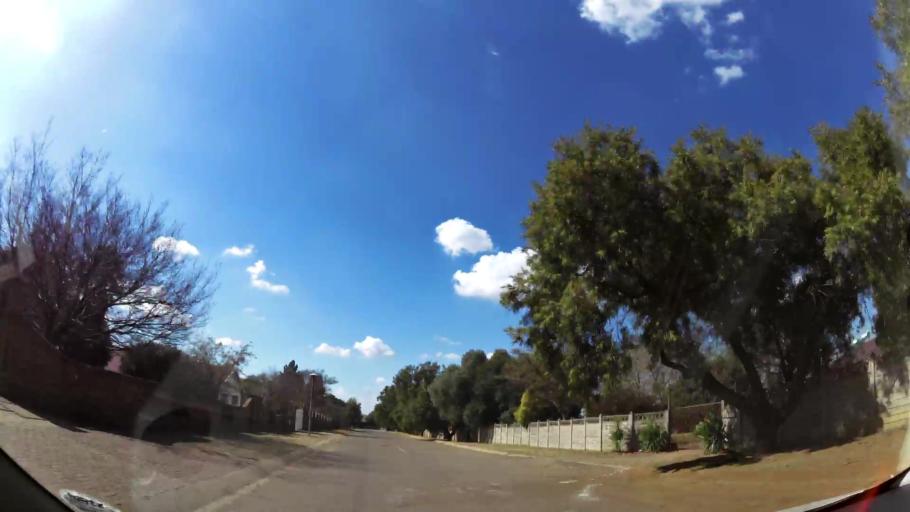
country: ZA
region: Mpumalanga
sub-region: Nkangala District Municipality
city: Witbank
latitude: -25.9474
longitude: 29.2474
